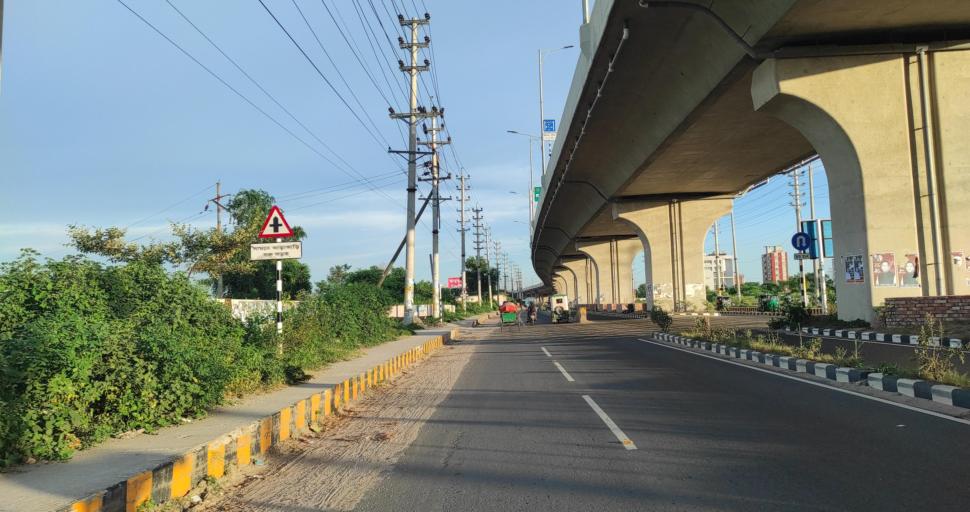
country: BD
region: Dhaka
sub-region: Dhaka
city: Dhaka
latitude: 23.6810
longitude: 90.4034
